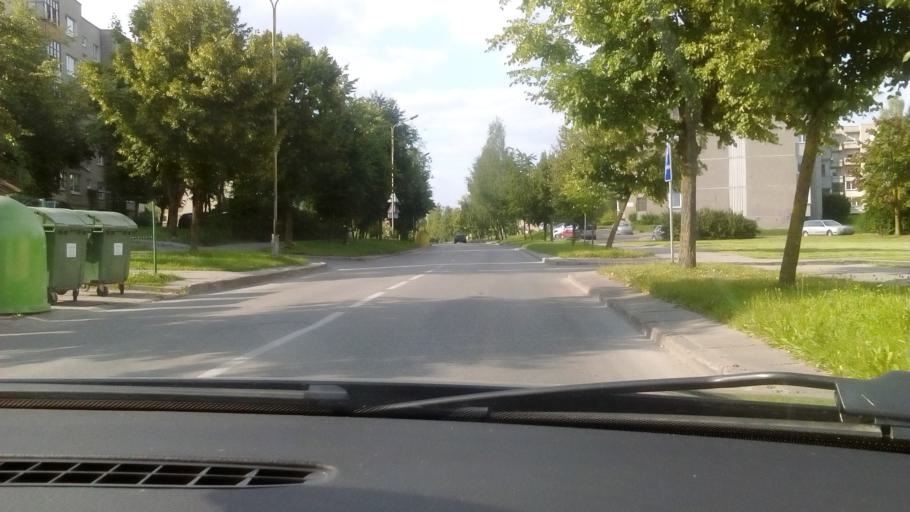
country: LT
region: Alytaus apskritis
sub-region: Alytus
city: Alytus
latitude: 54.3954
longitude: 24.0205
